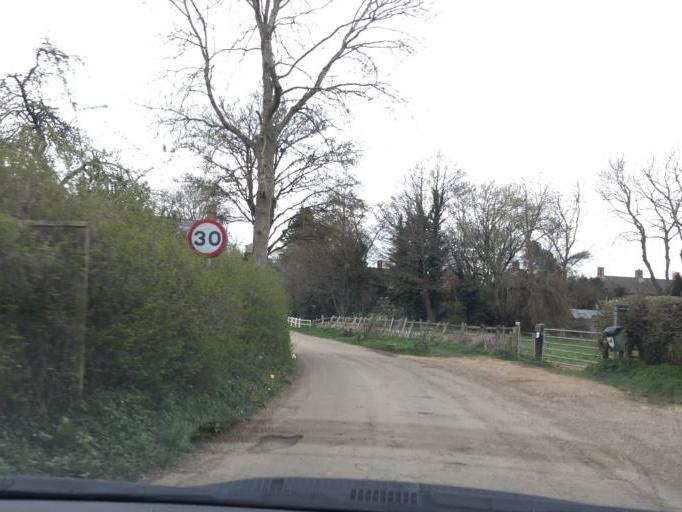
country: GB
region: England
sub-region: Oxfordshire
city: Hanwell
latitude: 52.0876
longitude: -1.3919
